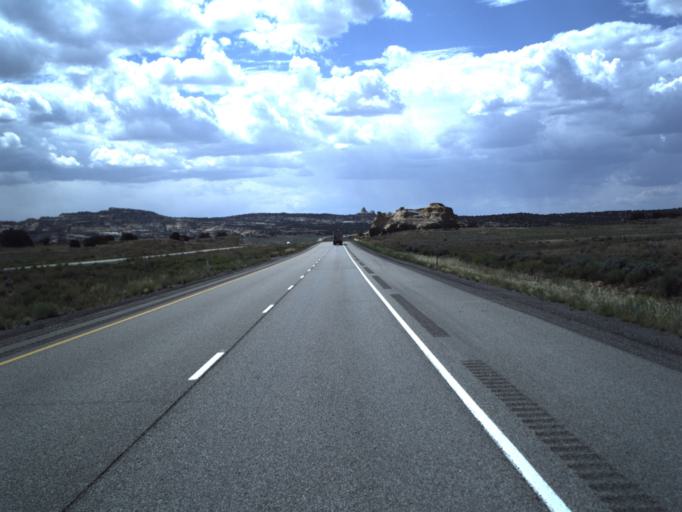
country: US
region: Utah
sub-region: Emery County
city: Castle Dale
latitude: 38.8713
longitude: -110.7669
